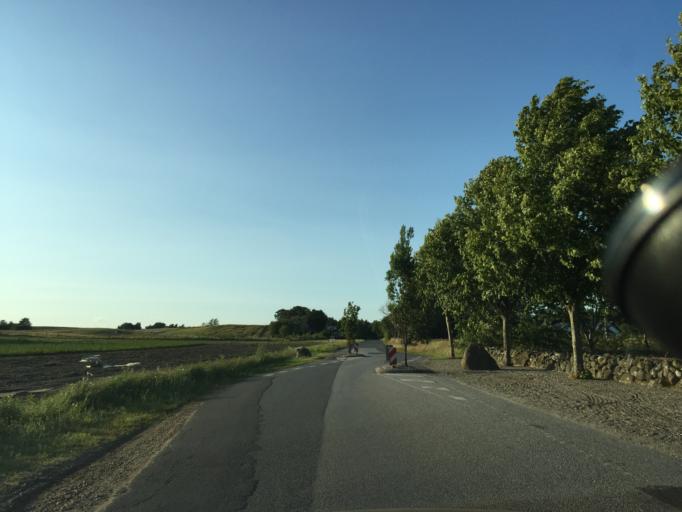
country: DK
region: Central Jutland
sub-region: Silkeborg Kommune
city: Svejbaek
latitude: 56.2255
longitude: 9.6656
